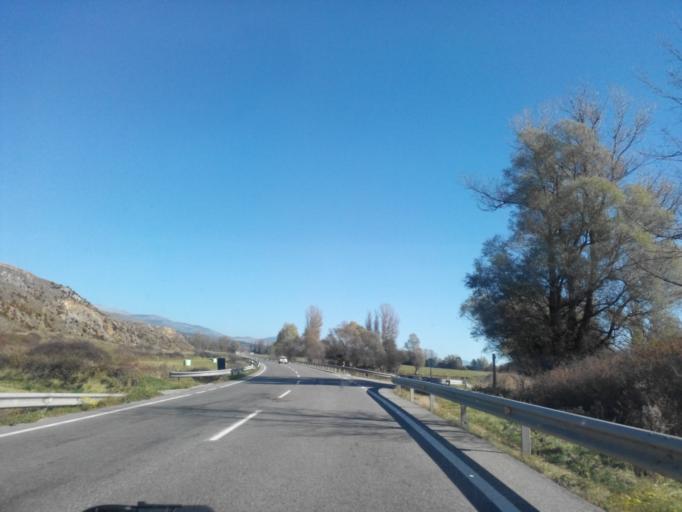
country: ES
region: Catalonia
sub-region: Provincia de Girona
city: Isovol
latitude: 42.3798
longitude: 1.8231
